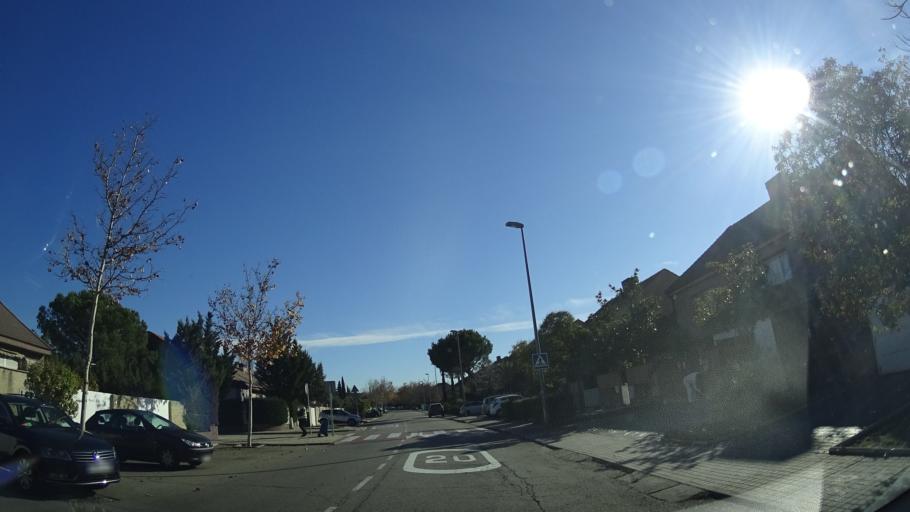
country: ES
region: Madrid
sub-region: Provincia de Madrid
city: Las Matas
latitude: 40.5221
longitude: -3.9118
